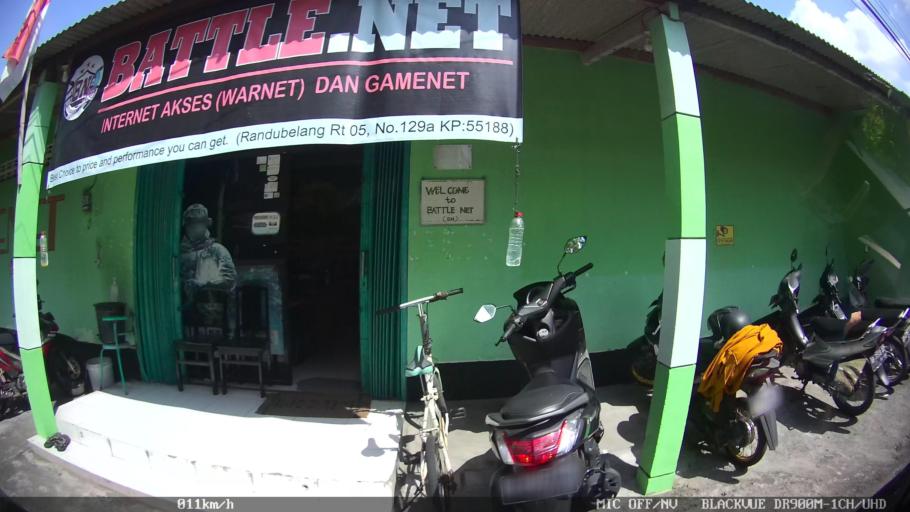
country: ID
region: Daerah Istimewa Yogyakarta
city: Kasihan
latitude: -7.8312
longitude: 110.3724
